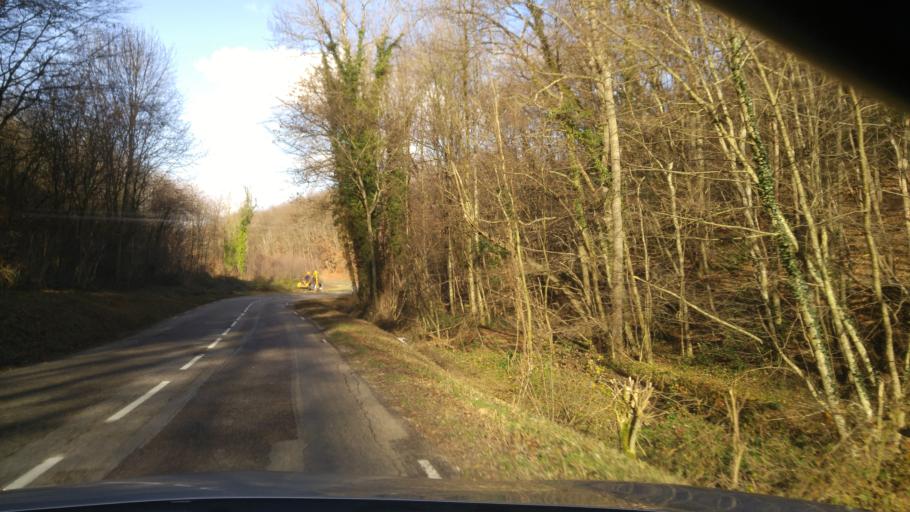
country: FR
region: Rhone-Alpes
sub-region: Departement de l'Isere
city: Roche
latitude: 45.5961
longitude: 5.1655
